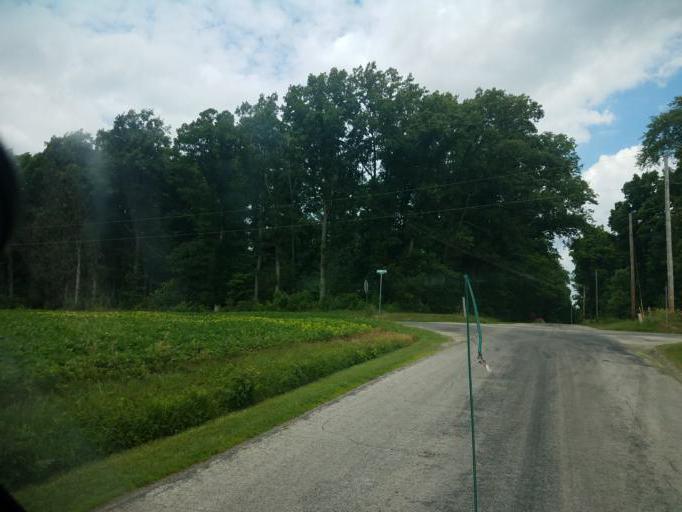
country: US
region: Ohio
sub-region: Huron County
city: Plymouth
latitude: 40.9445
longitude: -82.7050
